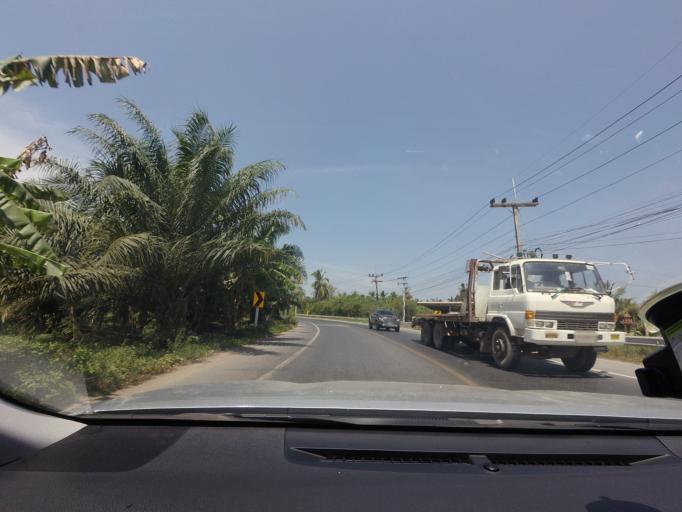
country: TH
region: Surat Thani
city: Phunphin
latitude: 9.1919
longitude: 99.2504
